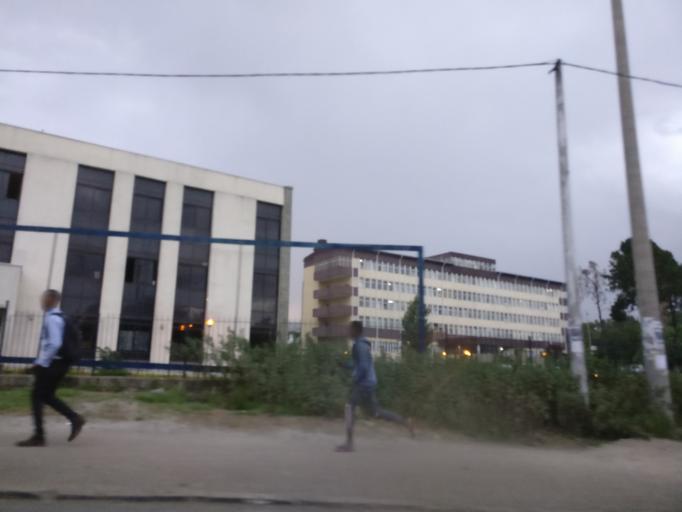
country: ET
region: Adis Abeba
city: Addis Ababa
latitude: 9.0176
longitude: 38.7561
